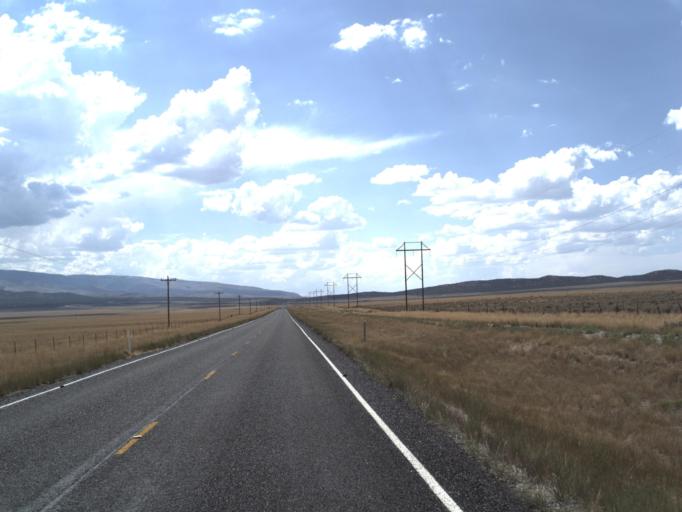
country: US
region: Idaho
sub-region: Power County
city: American Falls
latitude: 41.9663
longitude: -113.0703
